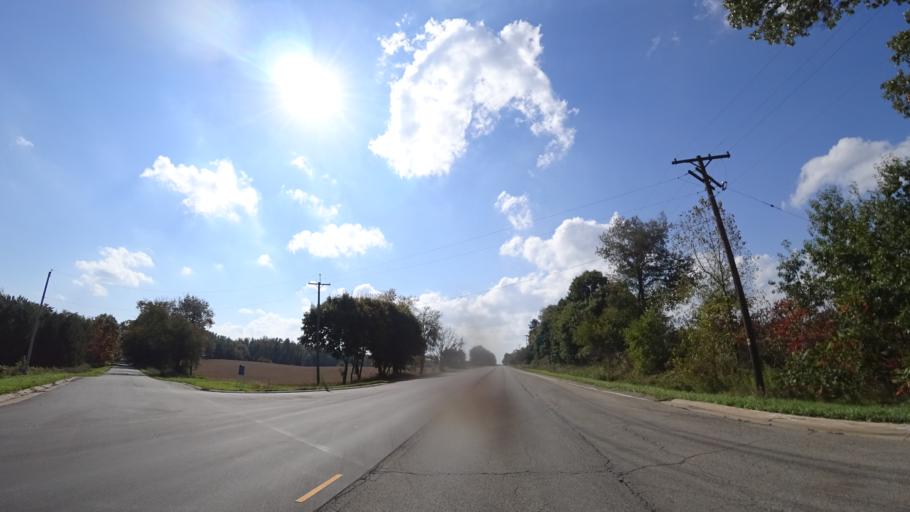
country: US
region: Michigan
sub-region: Calhoun County
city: Homer
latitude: 42.1249
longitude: -84.9340
